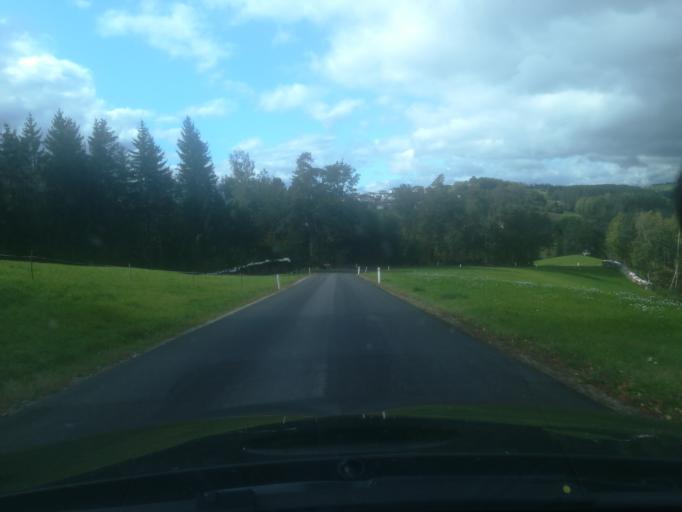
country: AT
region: Upper Austria
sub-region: Politischer Bezirk Urfahr-Umgebung
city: Herzogsdorf
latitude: 48.4254
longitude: 14.1411
